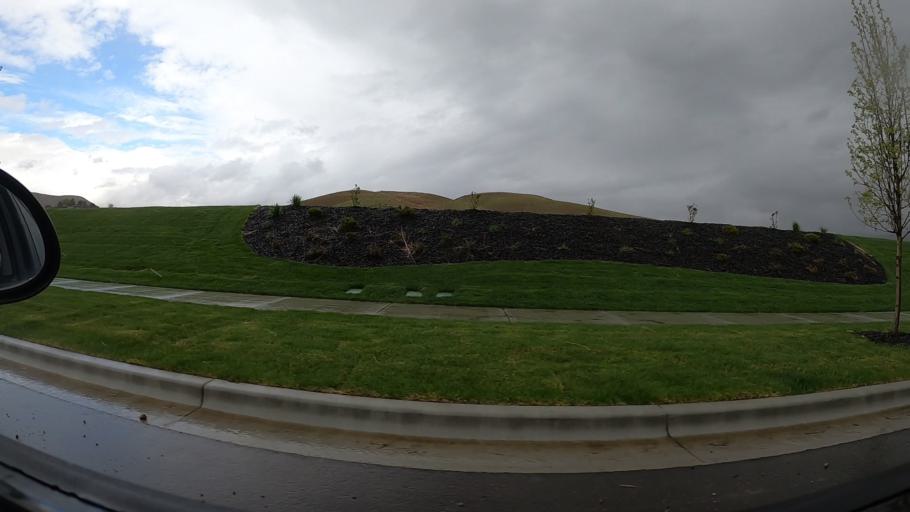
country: US
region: Idaho
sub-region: Ada County
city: Eagle
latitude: 43.7360
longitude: -116.2849
